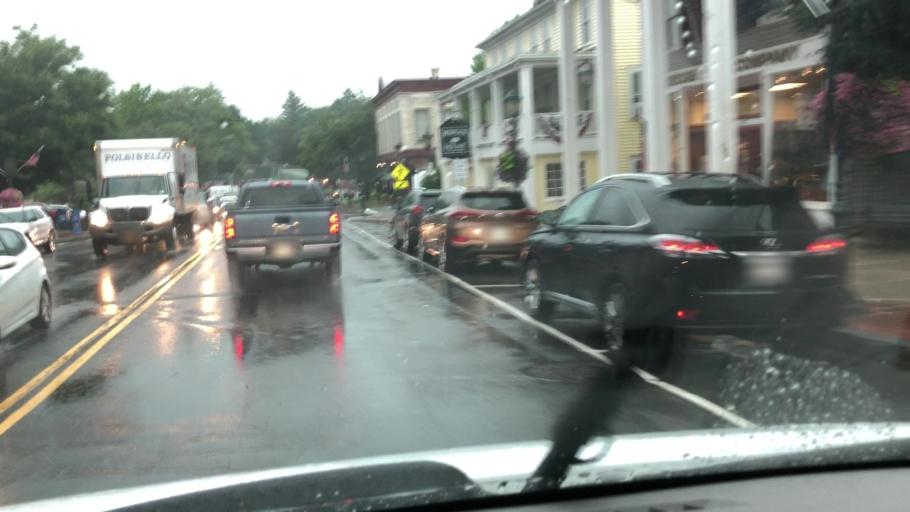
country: US
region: Massachusetts
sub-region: Berkshire County
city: Lee
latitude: 42.3053
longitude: -73.2493
